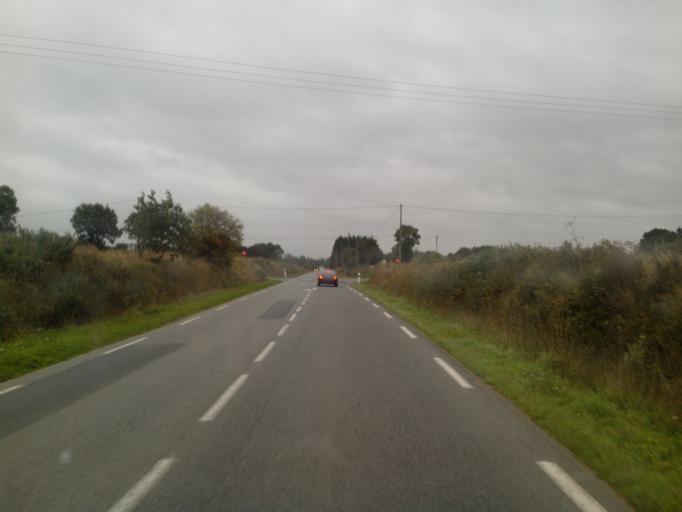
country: FR
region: Brittany
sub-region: Departement des Cotes-d'Armor
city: Plourivo
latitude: 48.7427
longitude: -3.0369
